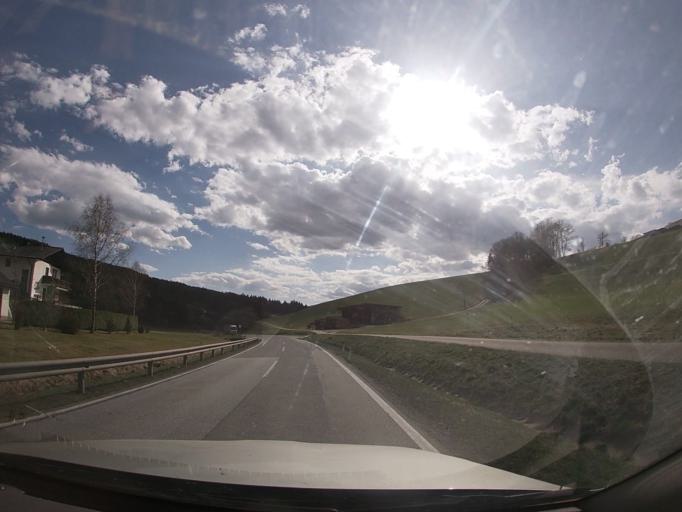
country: AT
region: Styria
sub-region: Politischer Bezirk Murau
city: Perchau am Sattel
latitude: 47.0971
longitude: 14.4506
